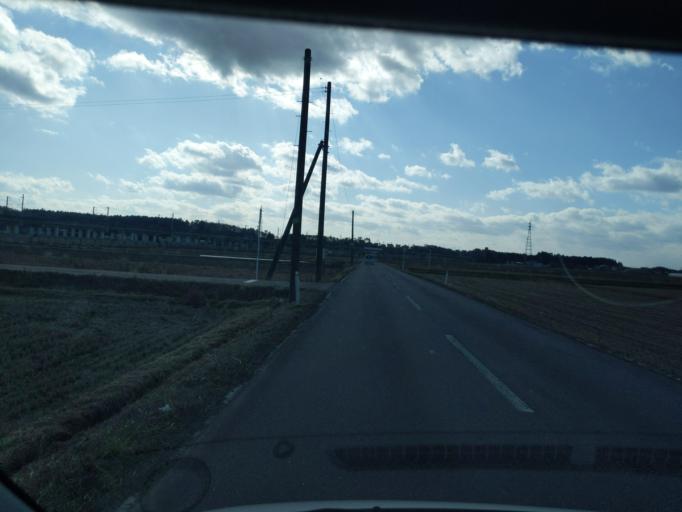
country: JP
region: Iwate
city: Ichinoseki
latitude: 38.7449
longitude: 141.0664
